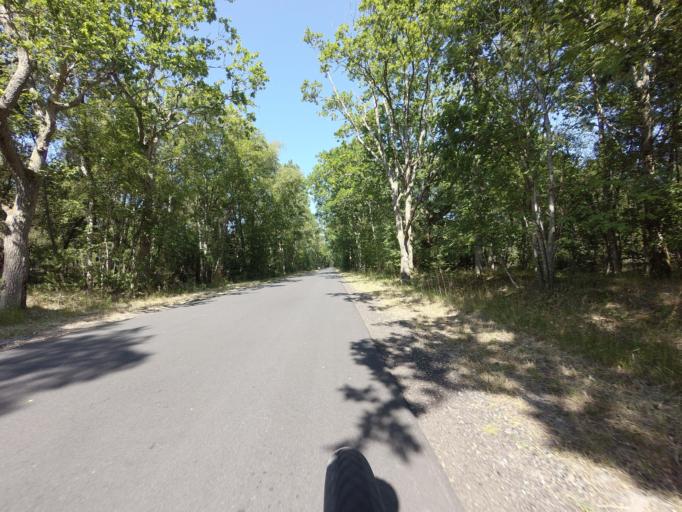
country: DK
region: North Denmark
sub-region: Laeso Kommune
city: Byrum
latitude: 57.2705
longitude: 11.0082
